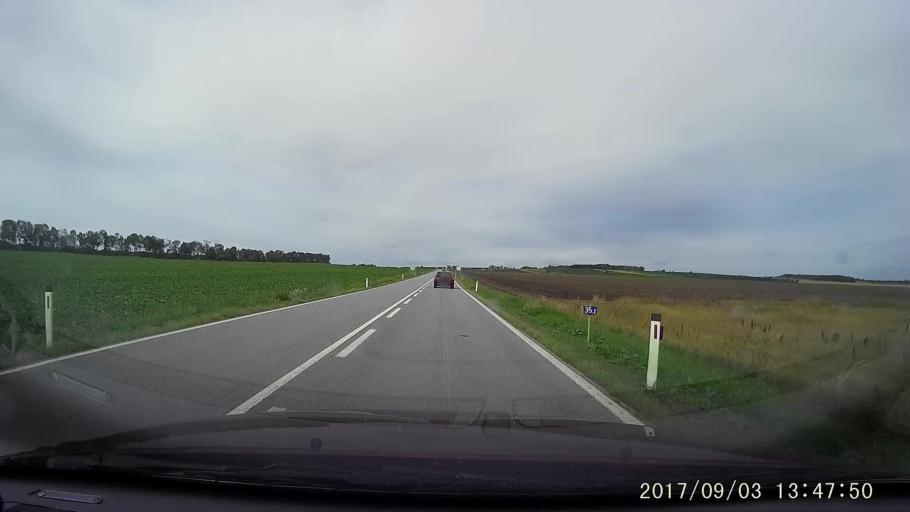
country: AT
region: Lower Austria
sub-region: Politischer Bezirk Hollabrunn
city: Guntersdorf
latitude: 48.6656
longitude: 16.0523
